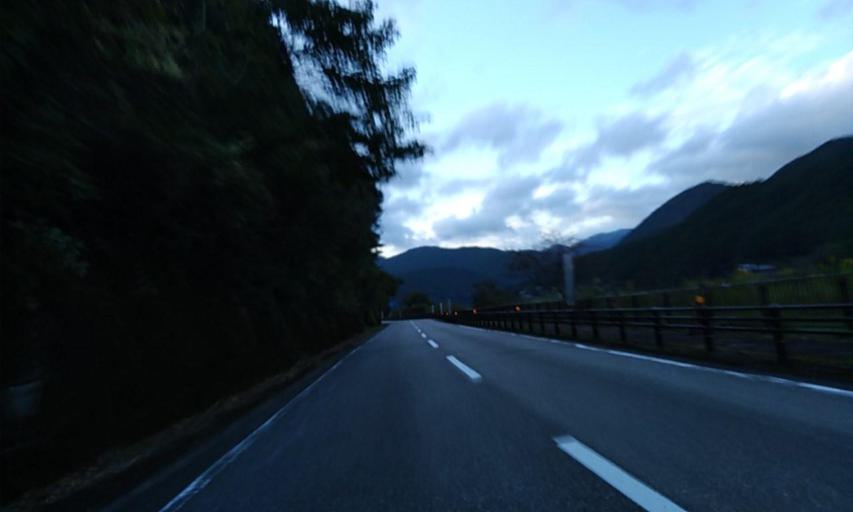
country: JP
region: Wakayama
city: Shingu
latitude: 33.7278
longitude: 135.9511
